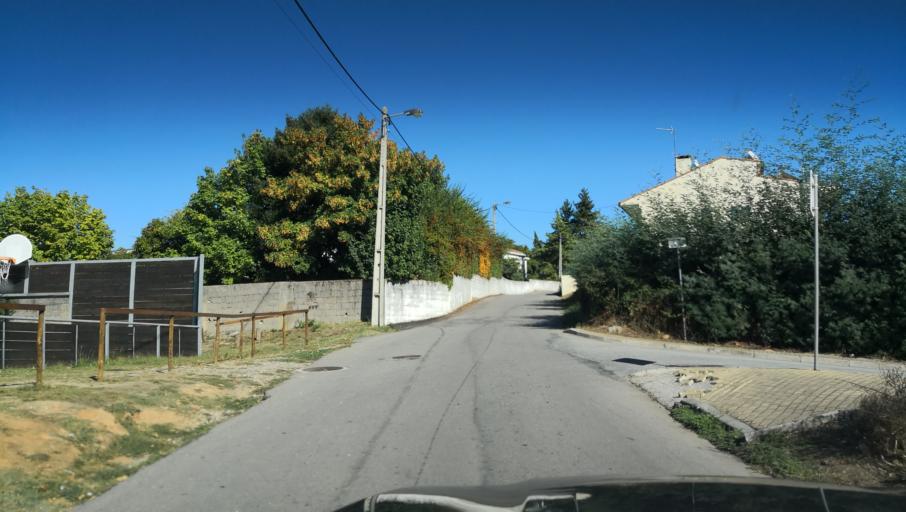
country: PT
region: Vila Real
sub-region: Vila Real
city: Vila Real
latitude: 41.2966
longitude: -7.7307
